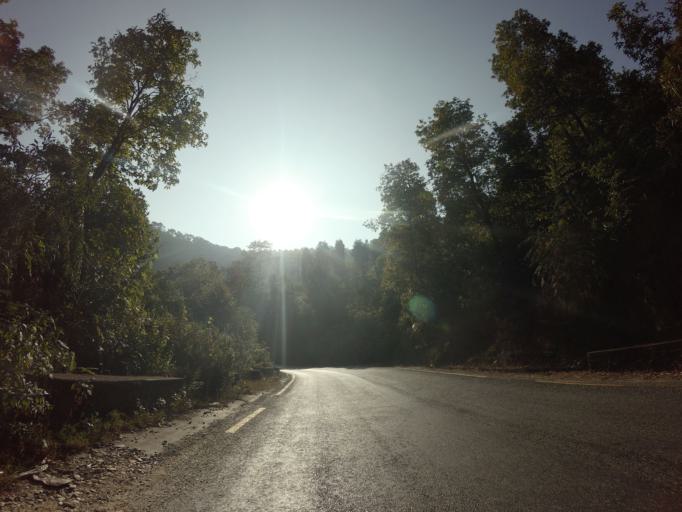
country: NP
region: Western Region
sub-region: Gandaki Zone
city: Pokhara
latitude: 28.1894
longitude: 83.9007
